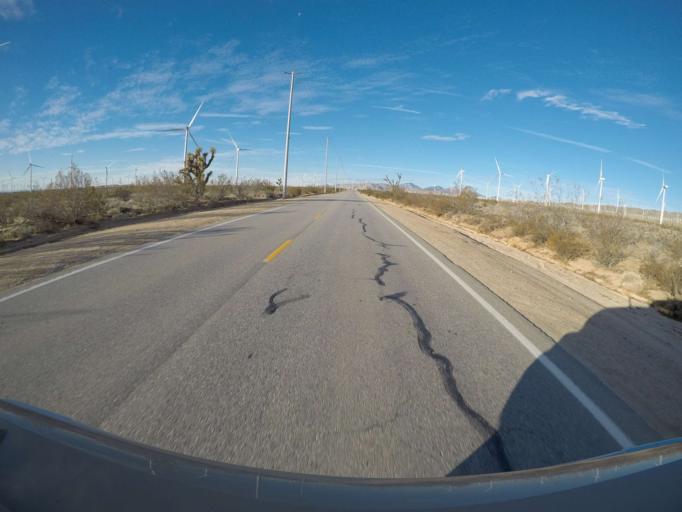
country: US
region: California
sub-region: Kern County
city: Mojave
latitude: 35.0437
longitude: -118.2272
